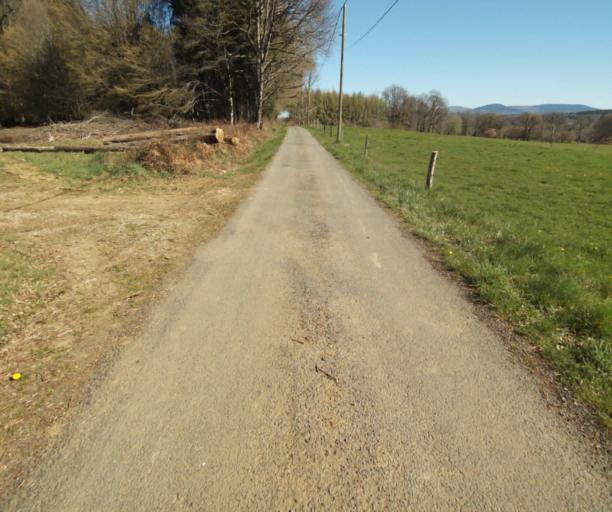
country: FR
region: Limousin
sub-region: Departement de la Correze
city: Seilhac
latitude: 45.3984
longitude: 1.7333
